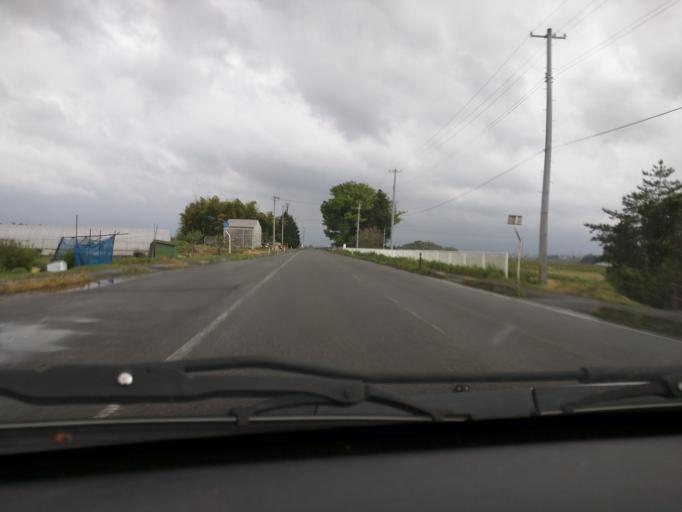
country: JP
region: Fukushima
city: Kitakata
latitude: 37.6220
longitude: 139.9186
